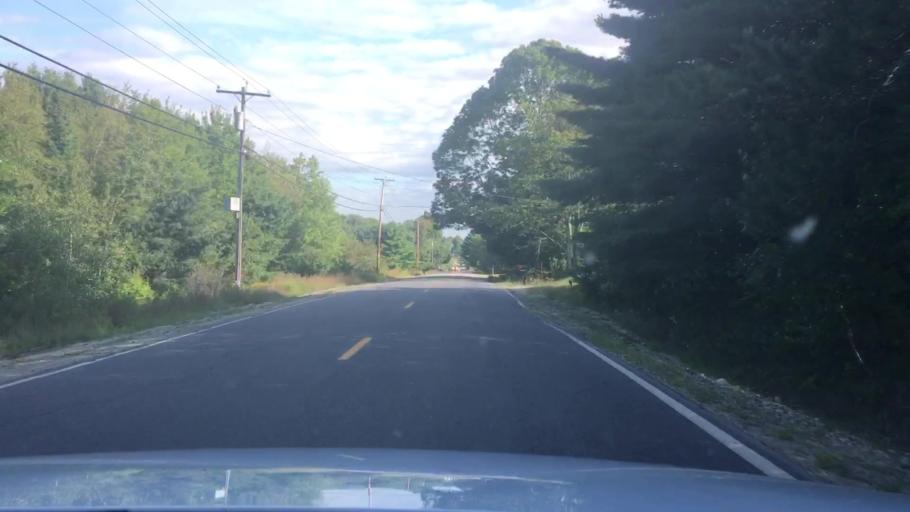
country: US
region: Maine
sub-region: Androscoggin County
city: Lisbon Falls
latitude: 43.9739
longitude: -70.0609
